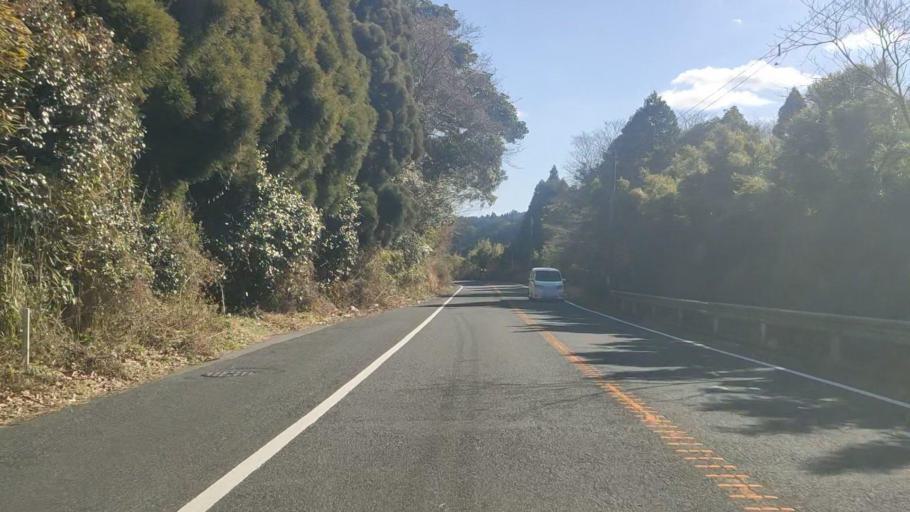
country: JP
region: Kagoshima
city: Sueyoshicho-ninokata
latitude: 31.6619
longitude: 130.8888
